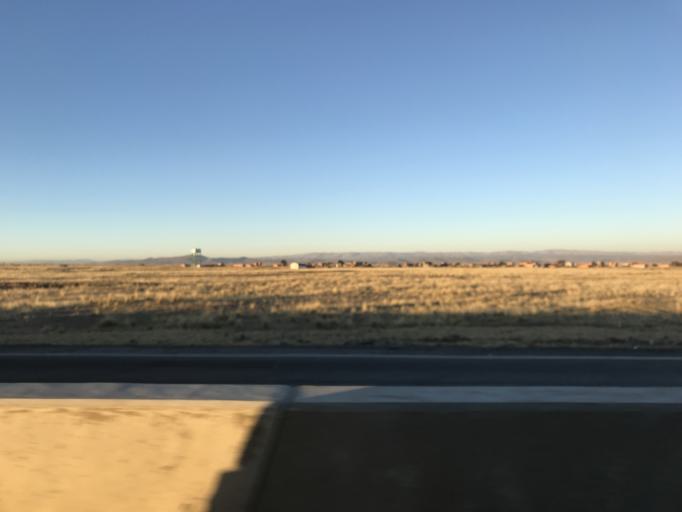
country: BO
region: La Paz
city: Batallas
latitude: -16.3103
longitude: -68.4587
